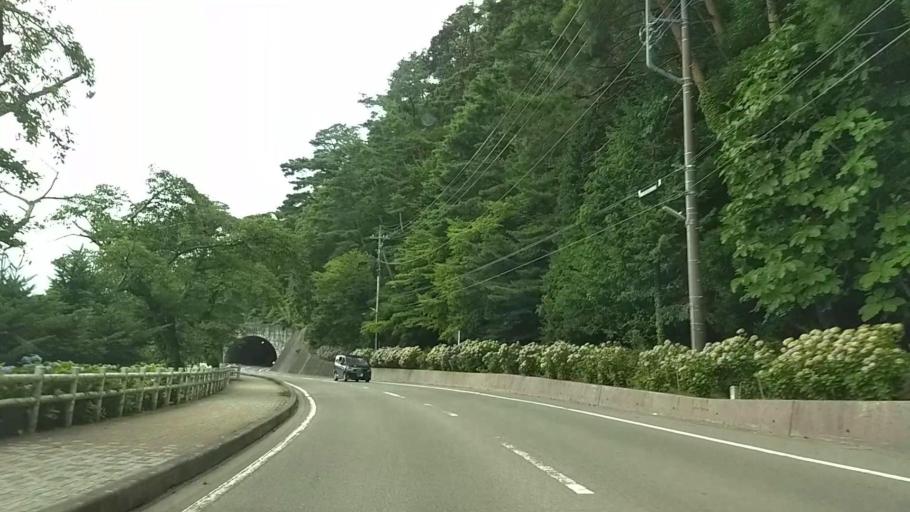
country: JP
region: Yamanashi
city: Fujikawaguchiko
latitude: 35.5245
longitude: 138.7581
